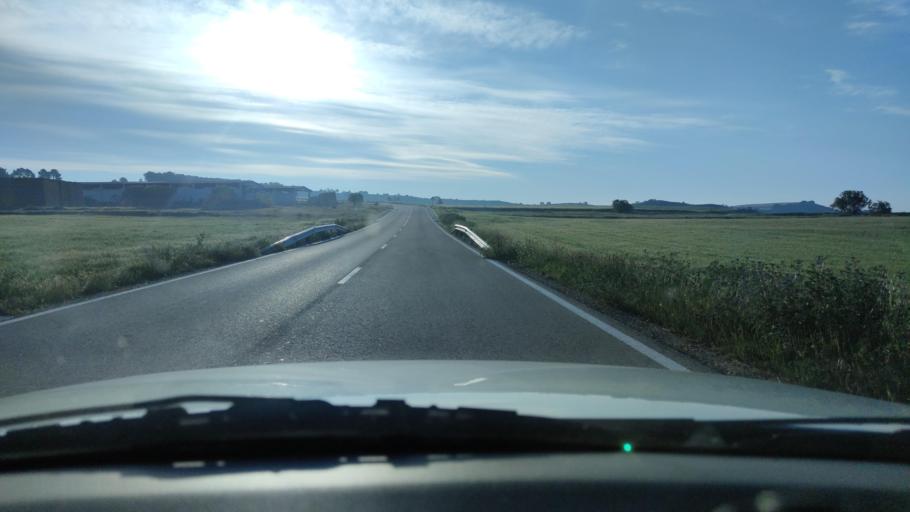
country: ES
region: Catalonia
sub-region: Provincia de Lleida
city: Castellsera
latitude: 41.7707
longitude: 1.0200
